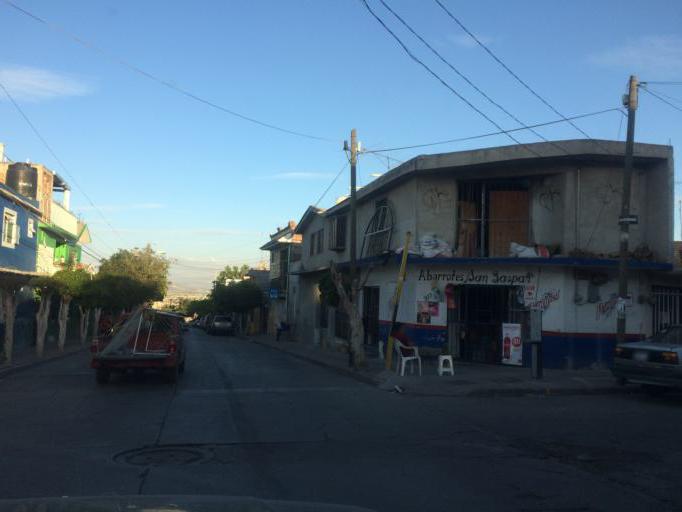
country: MX
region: Guanajuato
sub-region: Leon
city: La Ermita
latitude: 21.1362
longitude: -101.7067
